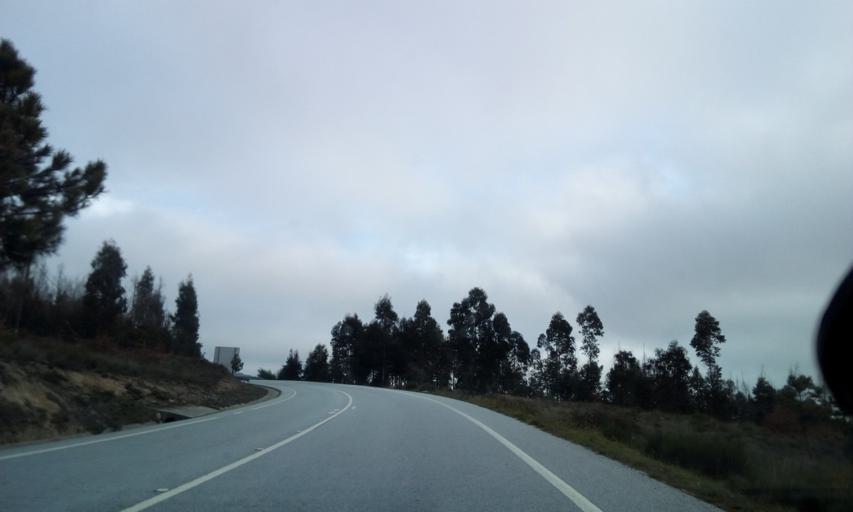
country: PT
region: Guarda
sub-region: Fornos de Algodres
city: Fornos de Algodres
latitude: 40.6656
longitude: -7.4751
